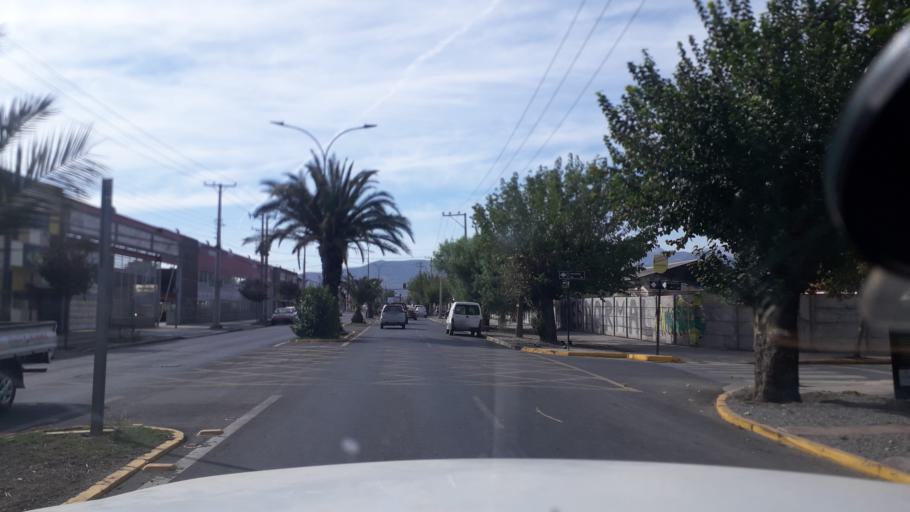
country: CL
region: Valparaiso
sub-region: Provincia de San Felipe
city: San Felipe
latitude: -32.7524
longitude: -70.7310
